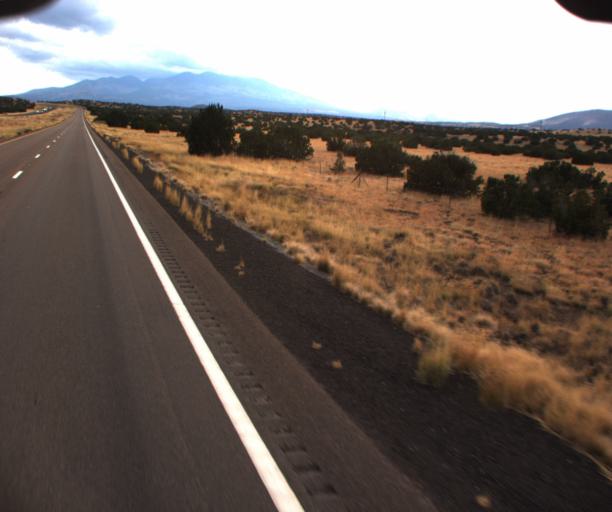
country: US
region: Arizona
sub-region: Coconino County
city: Flagstaff
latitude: 35.5014
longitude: -111.5510
